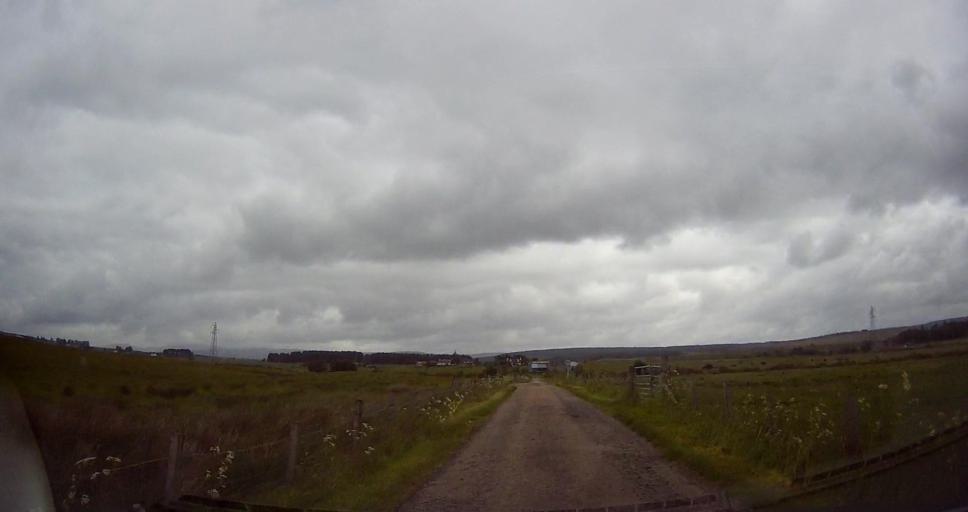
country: GB
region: Scotland
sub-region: Highland
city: Alness
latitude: 58.0587
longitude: -4.4322
